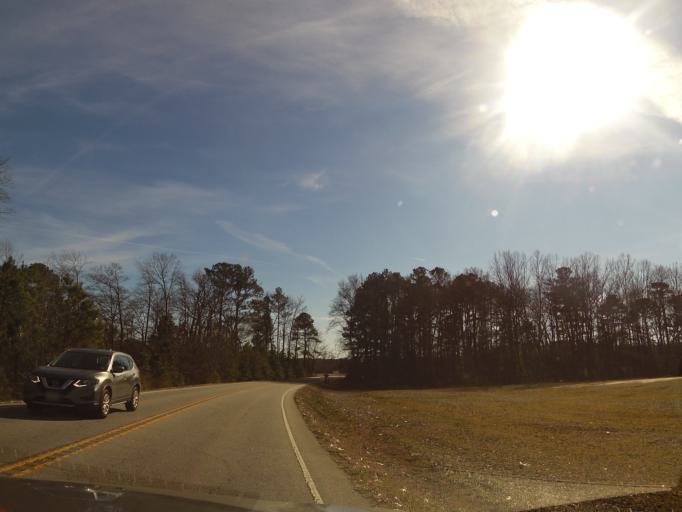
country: US
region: Virginia
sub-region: Isle of Wight County
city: Windsor
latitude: 36.8404
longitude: -76.7469
